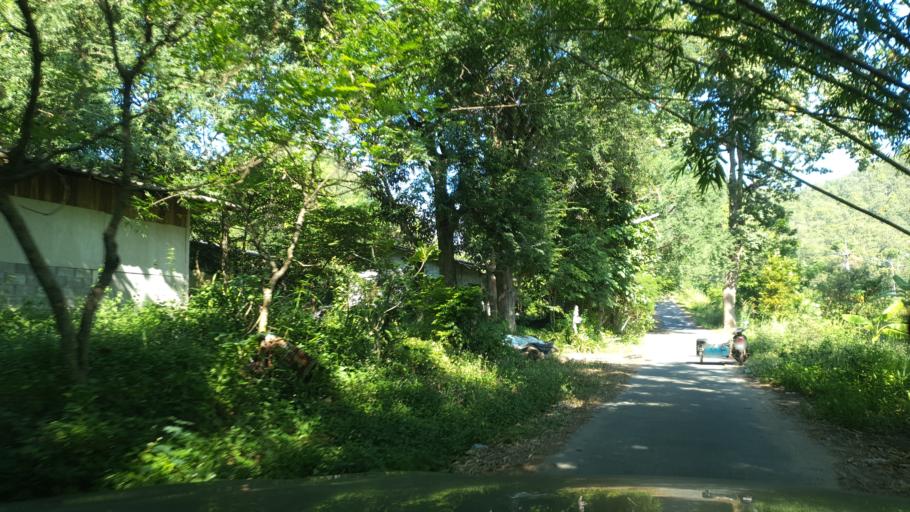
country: TH
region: Chiang Mai
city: San Sai
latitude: 18.8902
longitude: 99.1679
